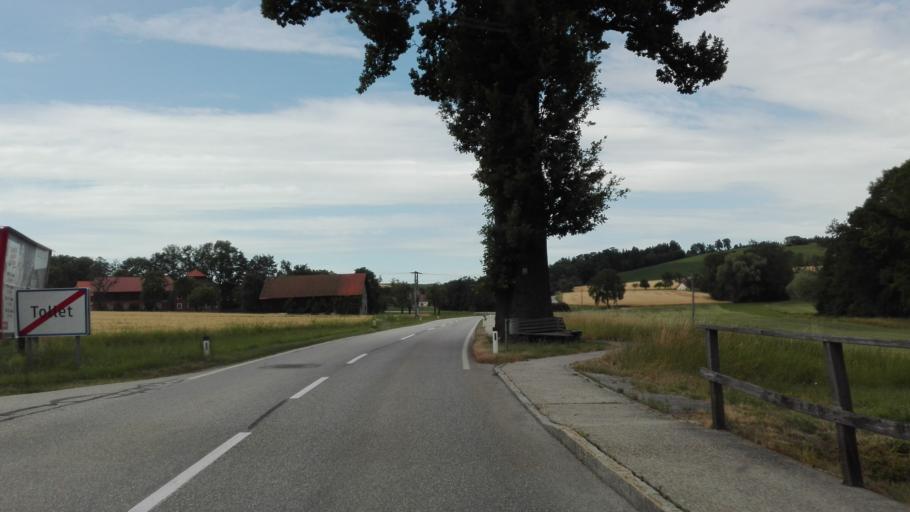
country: AT
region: Upper Austria
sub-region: Politischer Bezirk Grieskirchen
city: Grieskirchen
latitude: 48.2479
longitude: 13.8125
